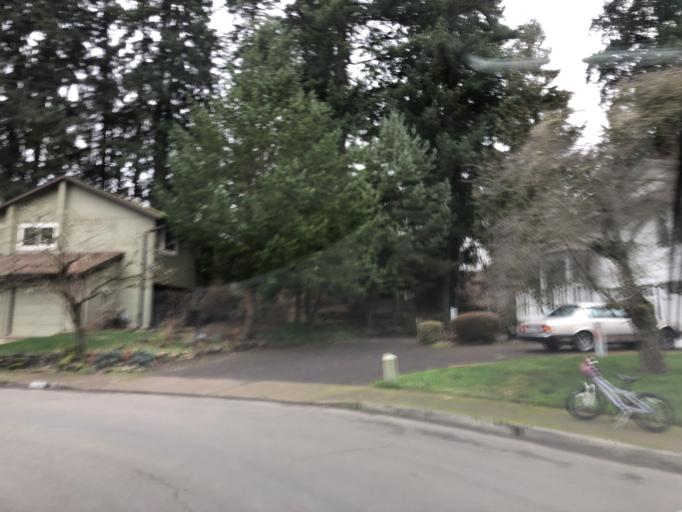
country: US
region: Oregon
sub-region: Washington County
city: Durham
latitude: 45.4180
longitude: -122.7599
